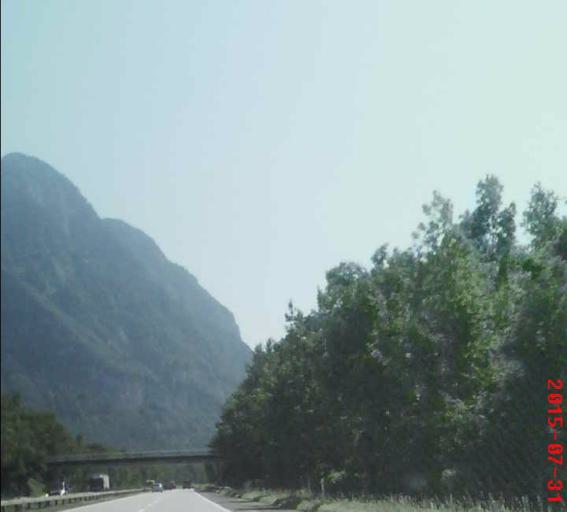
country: LI
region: Triesen
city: Triesen
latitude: 47.1115
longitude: 9.5166
